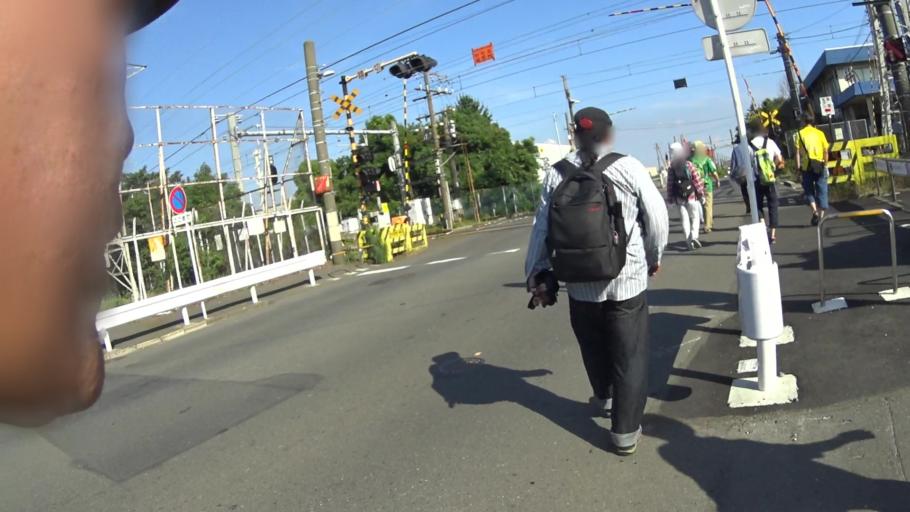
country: JP
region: Kanagawa
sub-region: Kawasaki-shi
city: Kawasaki
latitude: 35.4978
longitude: 139.6960
